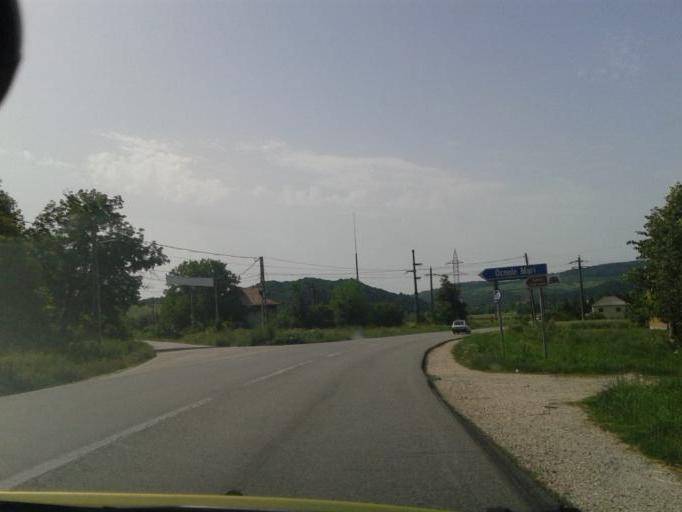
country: RO
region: Valcea
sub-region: Oras Baile Govora
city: Baile Govora
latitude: 45.0911
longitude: 24.2172
